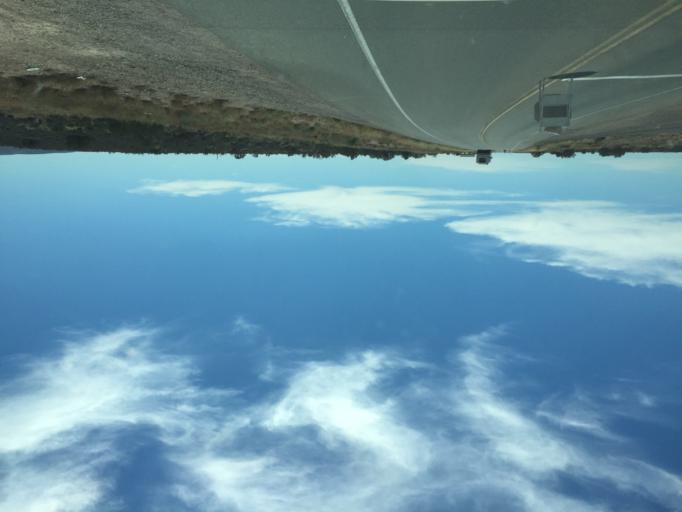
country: US
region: Arizona
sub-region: Mohave County
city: Meadview
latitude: 35.9851
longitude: -113.8214
